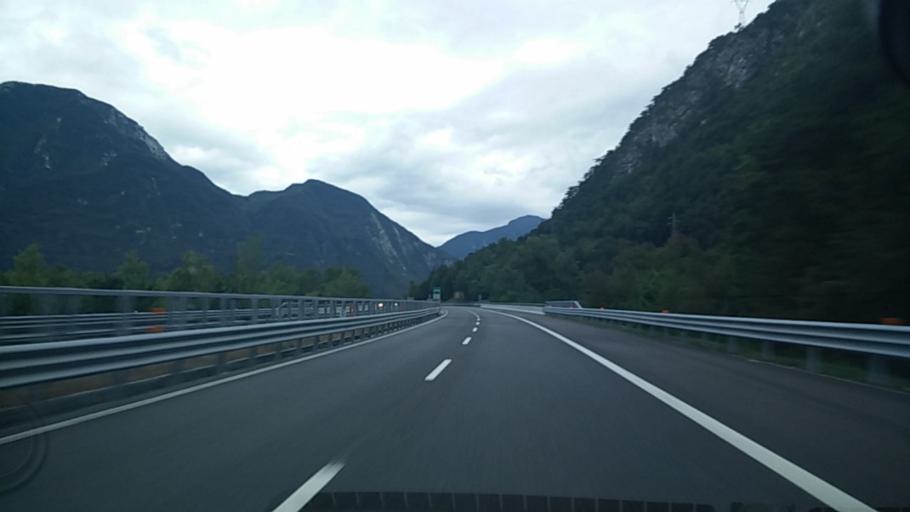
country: IT
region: Friuli Venezia Giulia
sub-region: Provincia di Udine
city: Amaro
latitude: 46.3851
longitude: 13.1230
